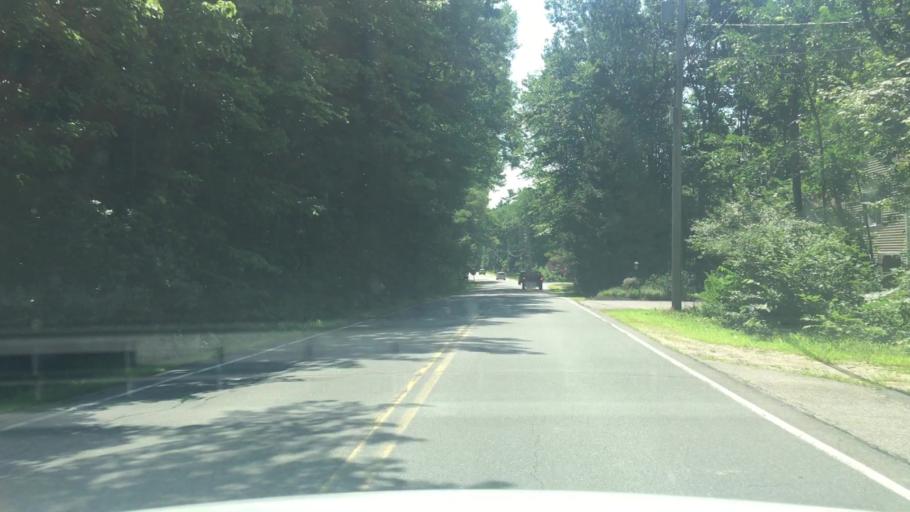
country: US
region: Maine
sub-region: Cumberland County
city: Cumberland Center
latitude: 43.8232
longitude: -70.3000
